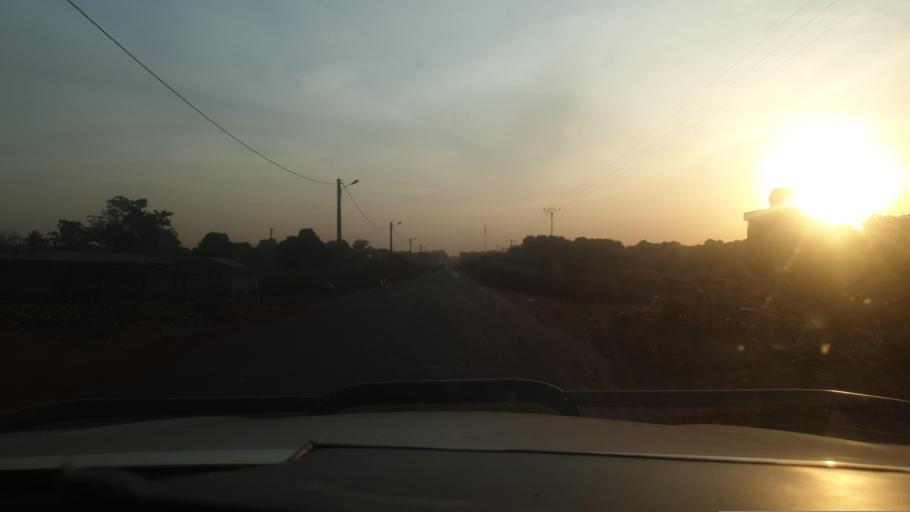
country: ML
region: Sikasso
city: Yanfolila
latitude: 11.1740
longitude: -8.1622
